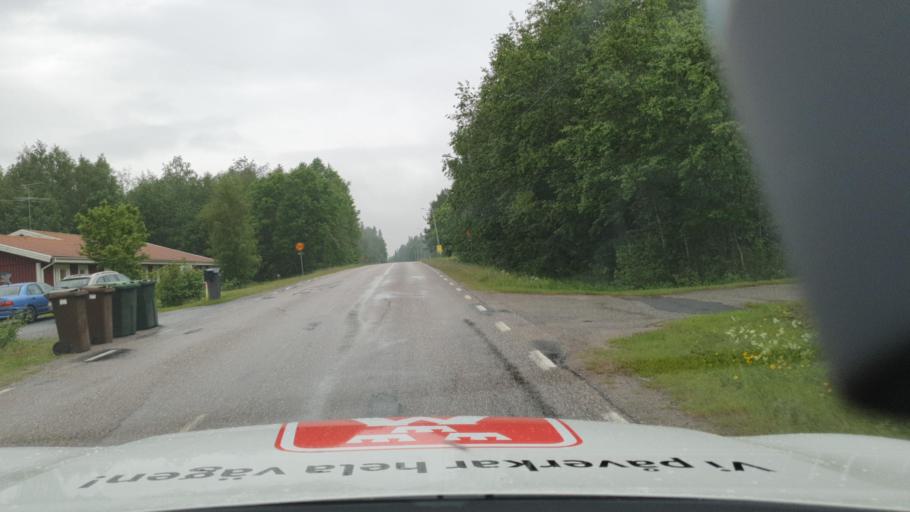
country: SE
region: Vaesterbotten
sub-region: Vannas Kommun
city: Vaennaes
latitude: 63.7702
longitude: 19.6194
